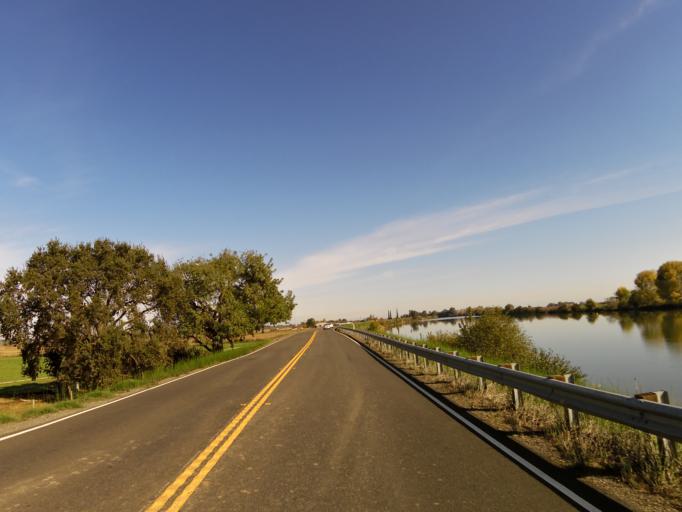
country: US
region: California
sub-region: Sacramento County
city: Walnut Grove
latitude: 38.1888
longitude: -121.5807
